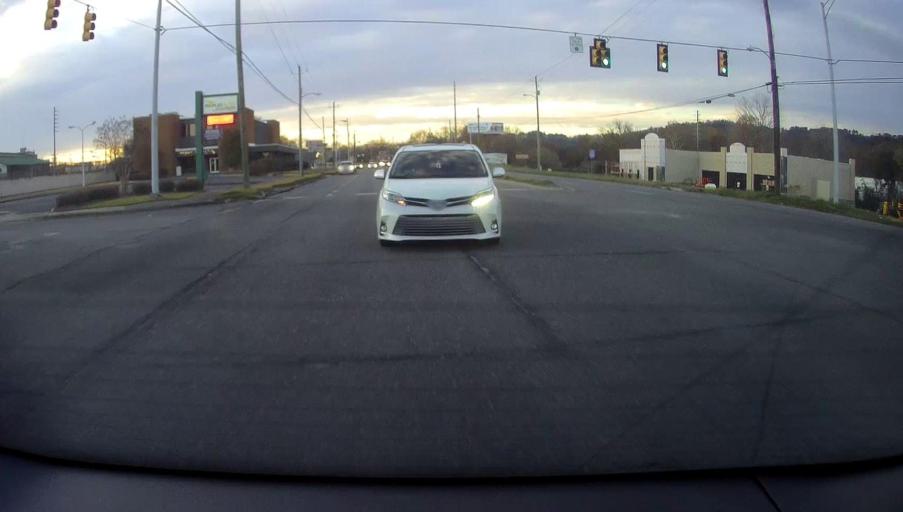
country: US
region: Alabama
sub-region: Etowah County
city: Gadsden
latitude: 34.0155
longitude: -86.0013
